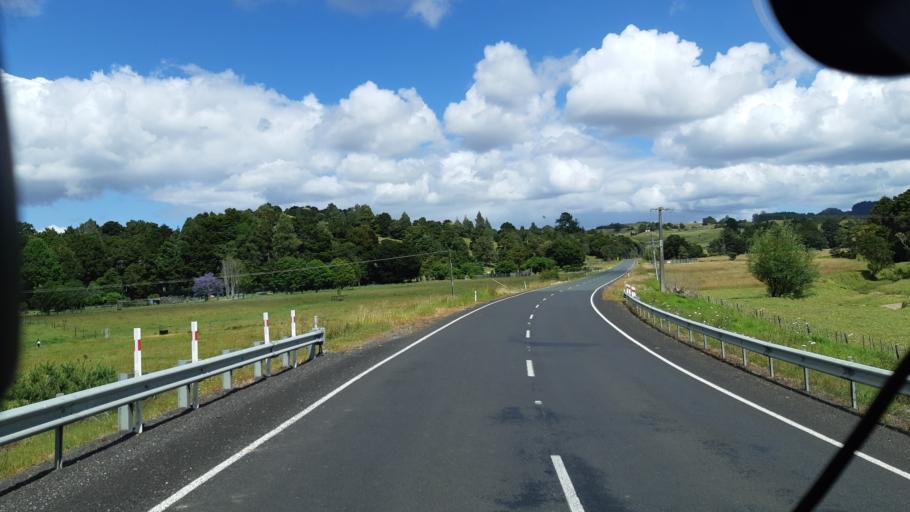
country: NZ
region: Northland
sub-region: Far North District
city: Waimate North
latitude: -35.2994
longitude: 173.6287
